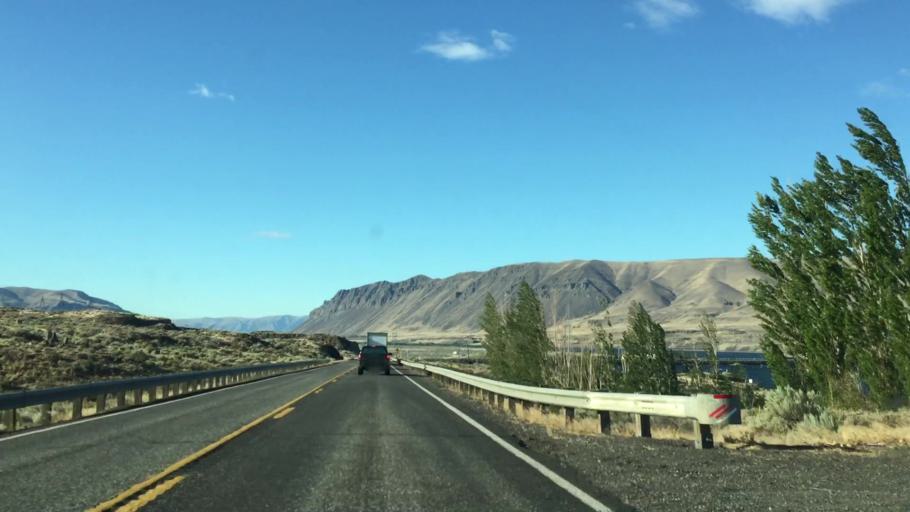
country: US
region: Washington
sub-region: Grant County
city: Mattawa
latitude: 46.8857
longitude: -119.9552
